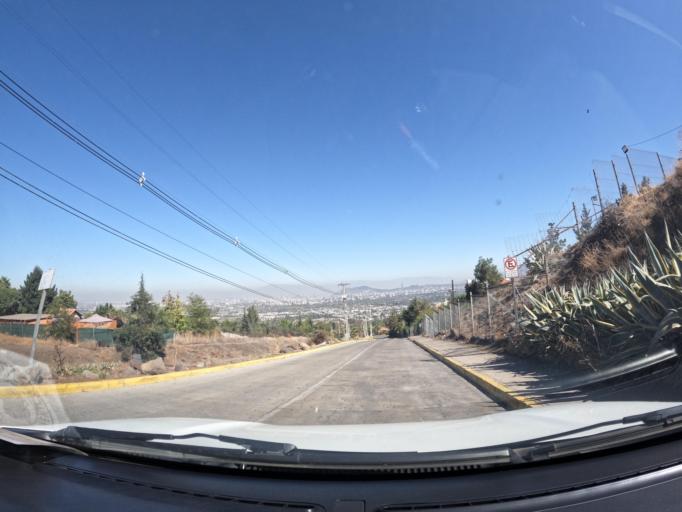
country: CL
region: Santiago Metropolitan
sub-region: Provincia de Santiago
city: Villa Presidente Frei, Nunoa, Santiago, Chile
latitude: -33.4647
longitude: -70.5175
